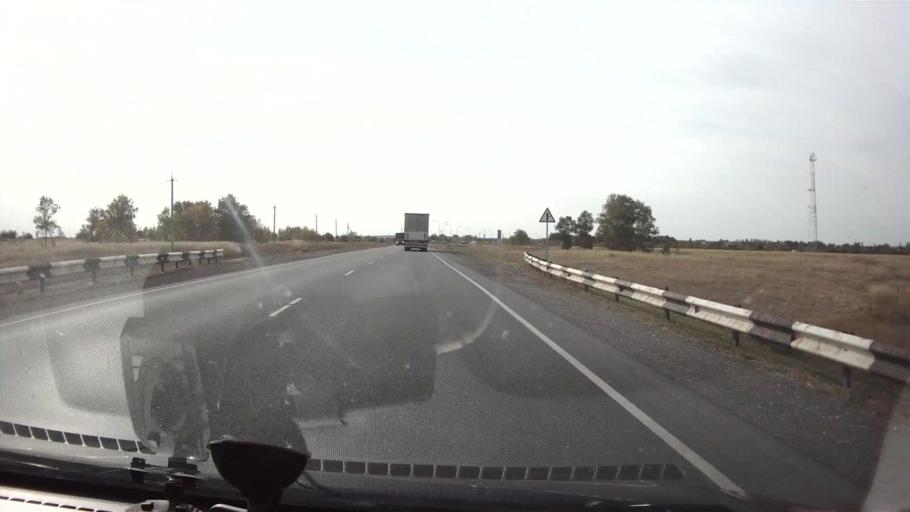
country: RU
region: Saratov
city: Sennoy
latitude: 52.1506
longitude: 46.9851
